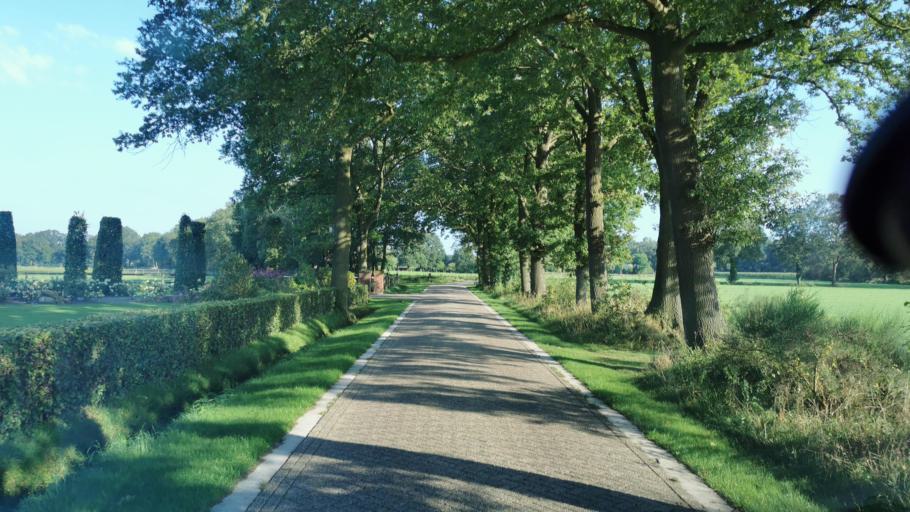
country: NL
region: Overijssel
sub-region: Gemeente Tubbergen
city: Tubbergen
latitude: 52.3468
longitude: 6.8390
